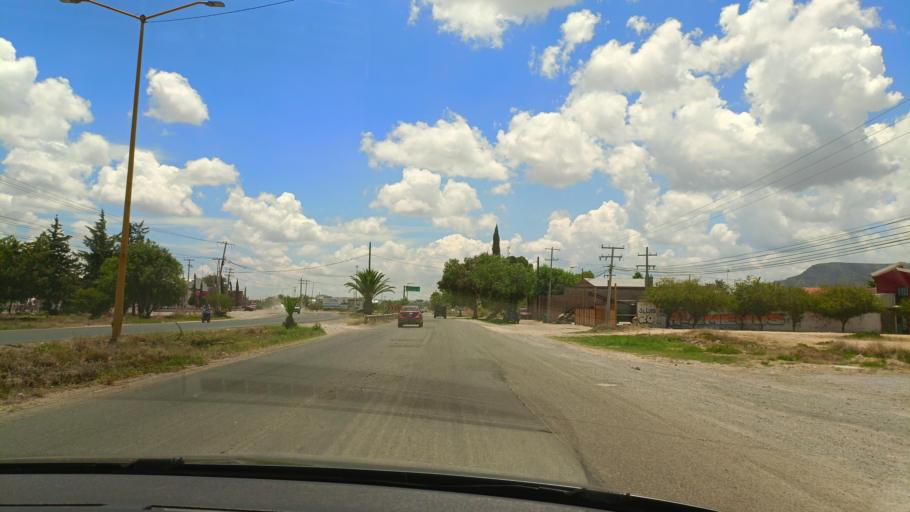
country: MX
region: Guanajuato
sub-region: San Luis de la Paz
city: San Ignacio
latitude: 21.2873
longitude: -100.5586
